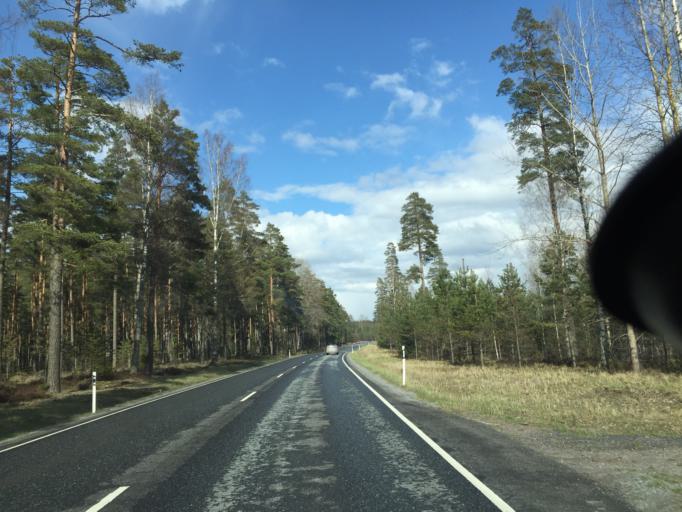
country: FI
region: Uusimaa
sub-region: Helsinki
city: Karjalohja
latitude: 60.1244
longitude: 23.8146
